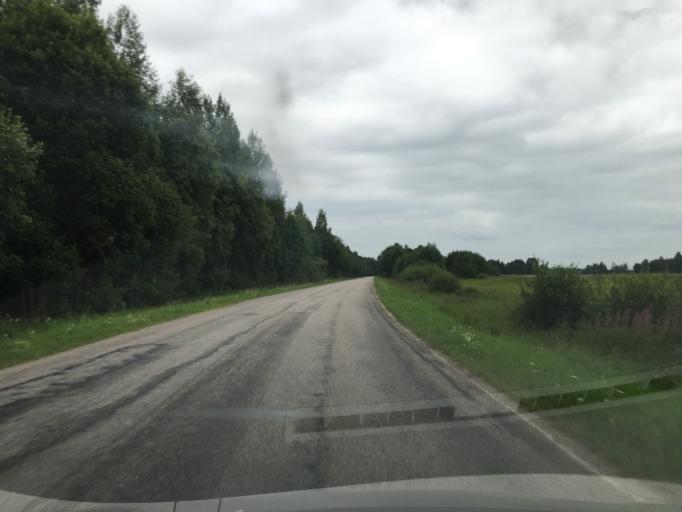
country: EE
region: Raplamaa
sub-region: Jaervakandi vald
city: Jarvakandi
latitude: 58.8049
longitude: 24.9200
